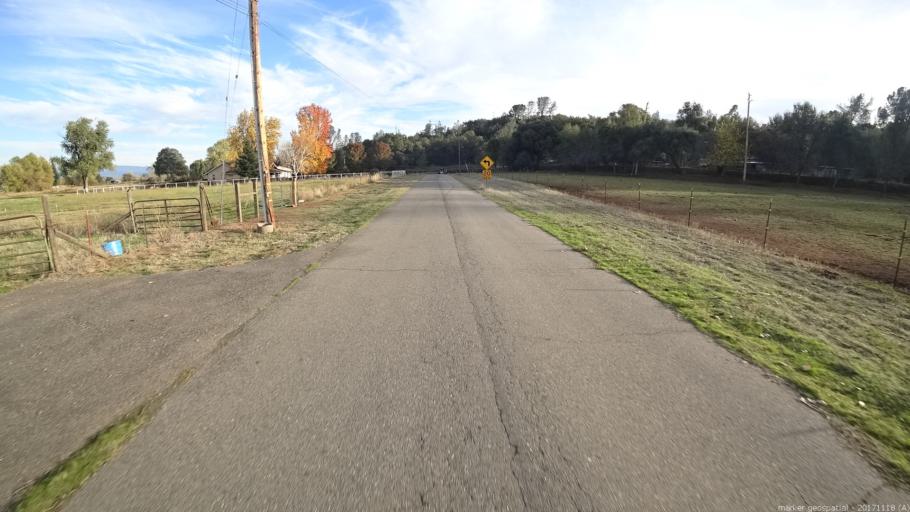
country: US
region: California
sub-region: Shasta County
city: Anderson
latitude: 40.4565
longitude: -122.3321
